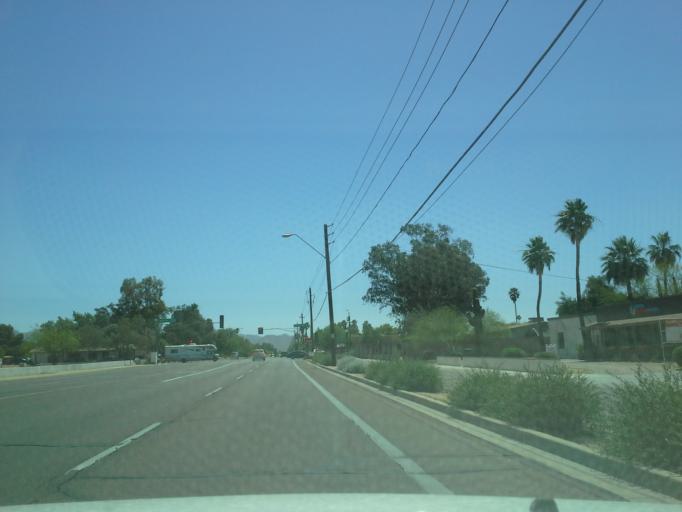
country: US
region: Arizona
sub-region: Maricopa County
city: Paradise Valley
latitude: 33.6113
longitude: -111.9446
